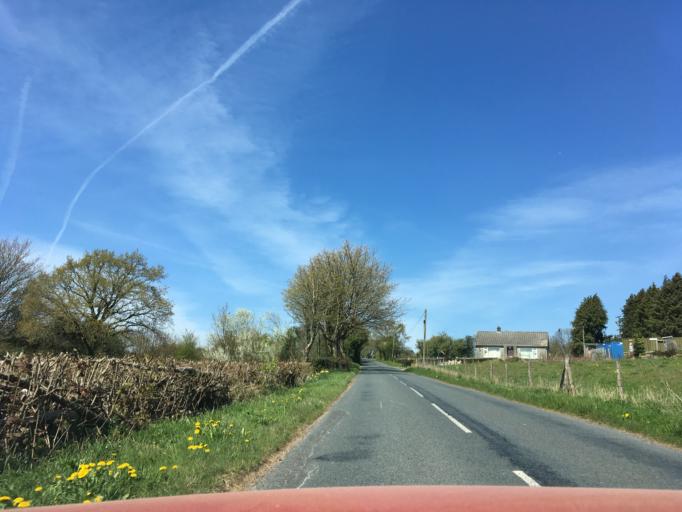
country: GB
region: Wales
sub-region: Newport
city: Llanvaches
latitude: 51.6483
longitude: -2.7764
